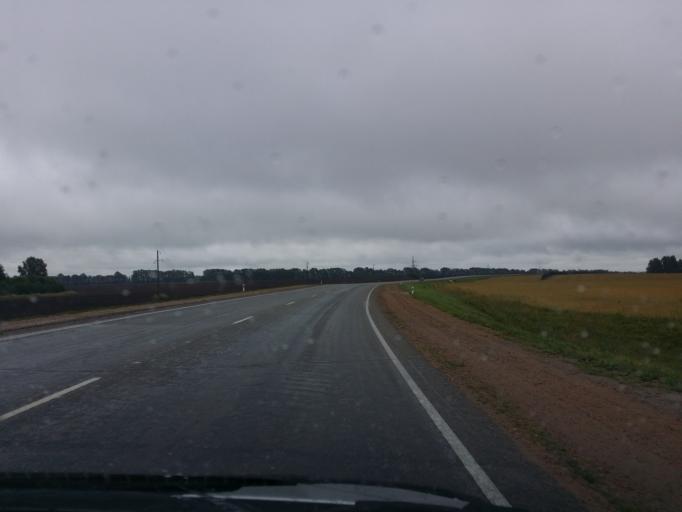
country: RU
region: Altai Krai
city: Nalobikha
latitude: 53.2463
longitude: 84.5831
